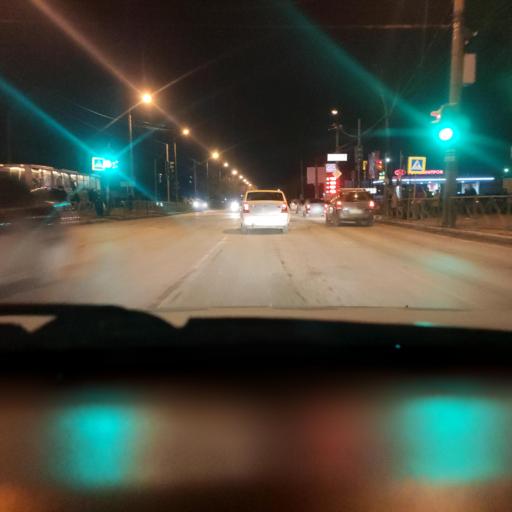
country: RU
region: Perm
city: Perm
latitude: 57.9726
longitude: 56.2462
